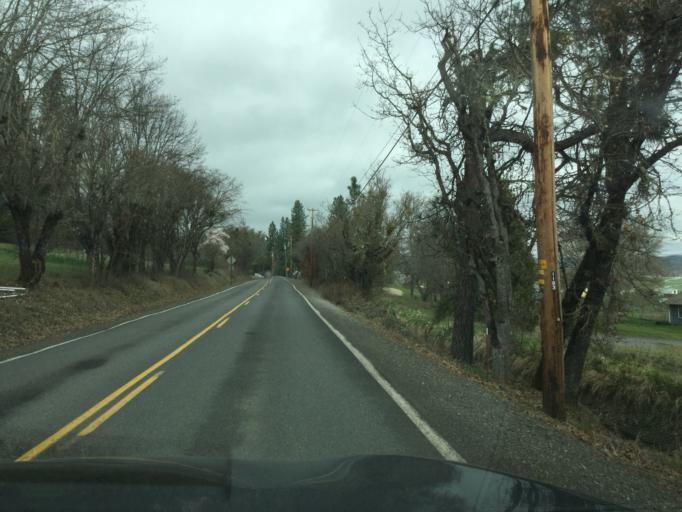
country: US
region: Oregon
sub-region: Jackson County
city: Central Point
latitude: 42.3747
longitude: -122.9528
